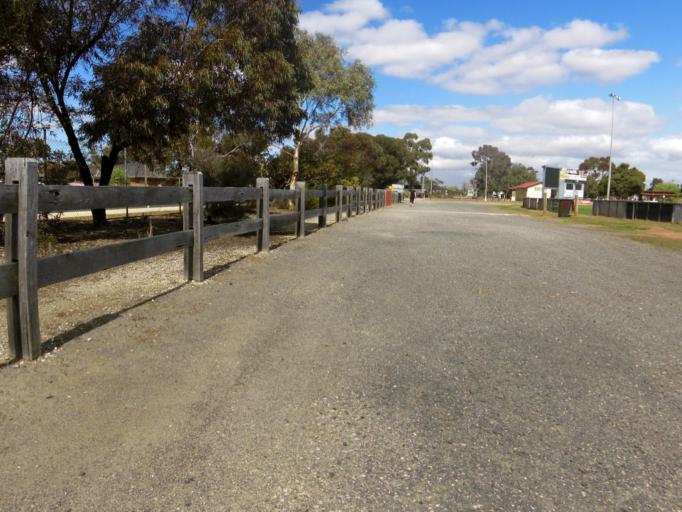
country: AU
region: Victoria
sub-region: Moorabool
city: Bacchus Marsh
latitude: -37.6576
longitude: 144.4423
